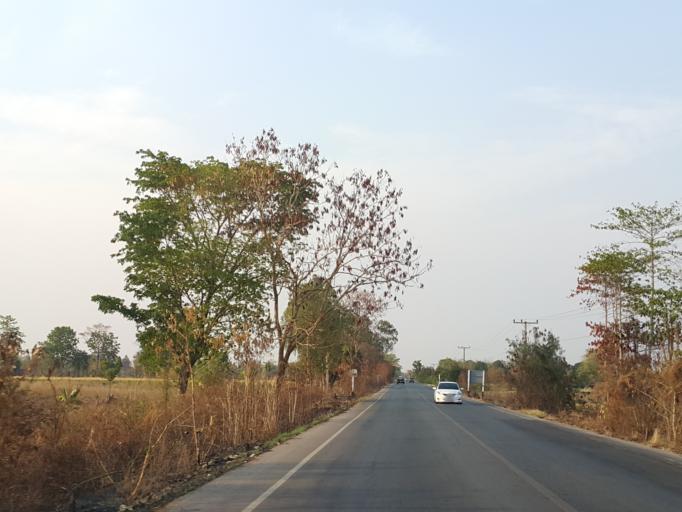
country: TH
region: Sukhothai
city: Si Samrong
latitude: 17.2121
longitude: 99.9487
